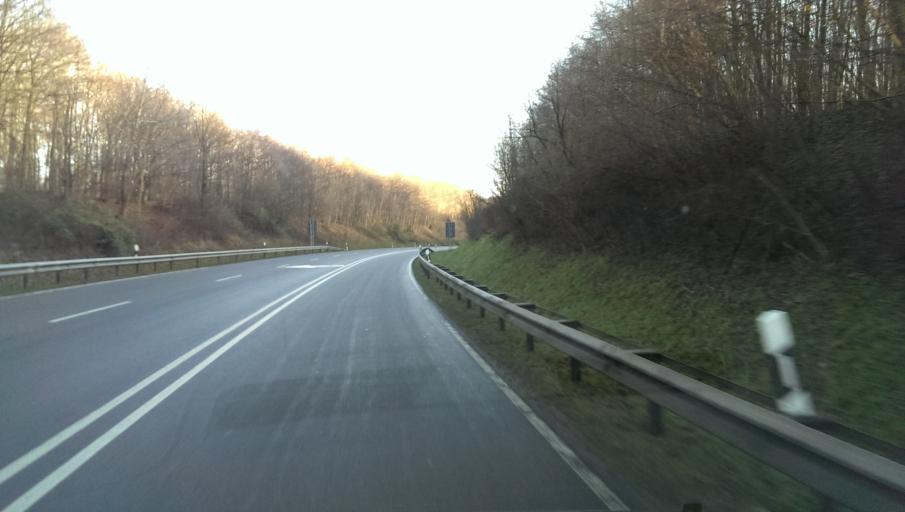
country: DE
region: North Rhine-Westphalia
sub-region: Regierungsbezirk Detmold
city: Bad Driburg
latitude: 51.7406
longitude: 8.9887
